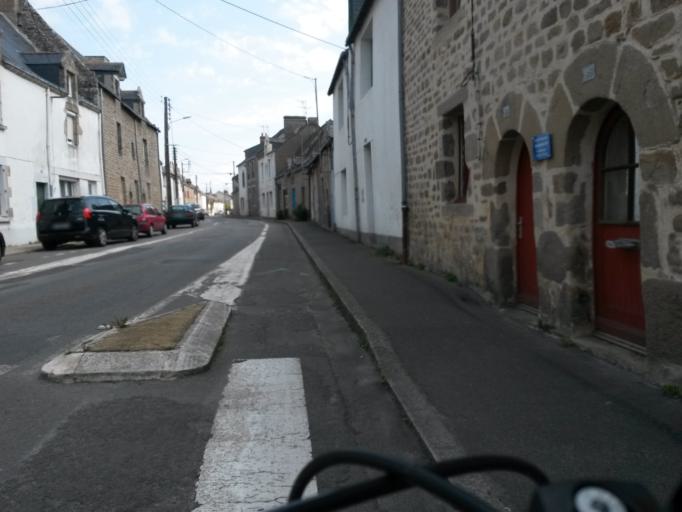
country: FR
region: Pays de la Loire
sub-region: Departement de la Loire-Atlantique
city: Guerande
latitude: 47.3273
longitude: -2.4387
